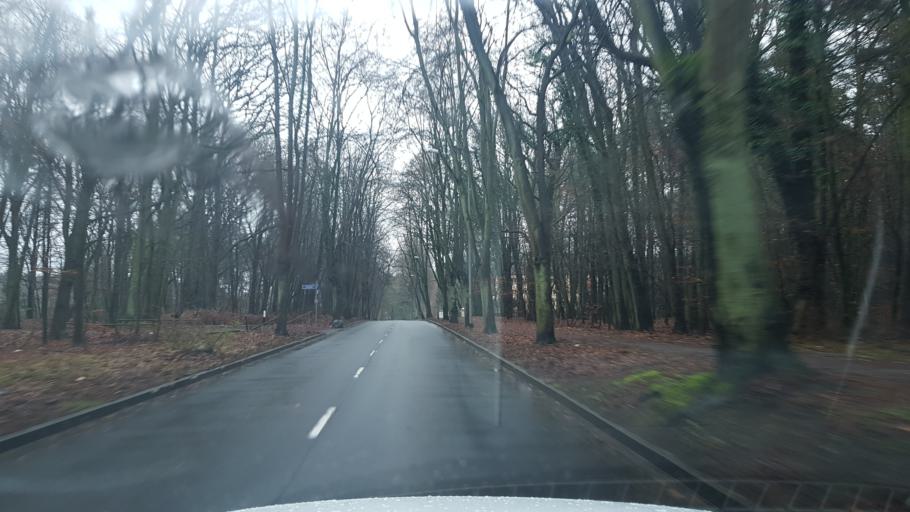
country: PL
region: West Pomeranian Voivodeship
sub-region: Powiat gryfinski
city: Stare Czarnowo
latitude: 53.3424
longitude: 14.7628
